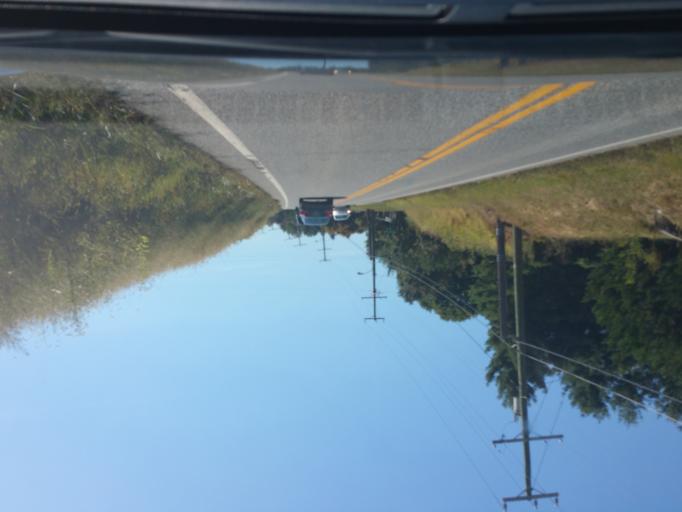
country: US
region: Maryland
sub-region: Harford County
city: Aberdeen
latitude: 39.5880
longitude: -76.1846
